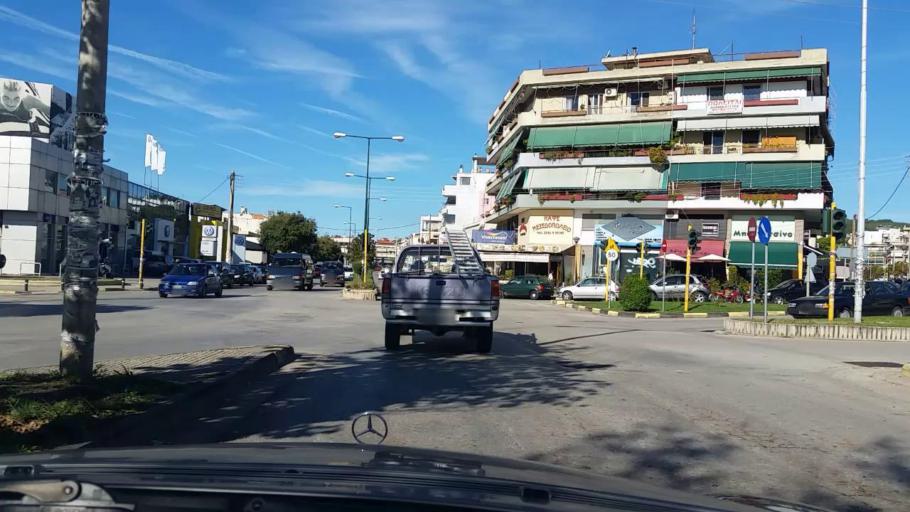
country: GR
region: Central Greece
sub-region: Nomos Fthiotidos
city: Lamia
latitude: 38.8942
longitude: 22.4451
